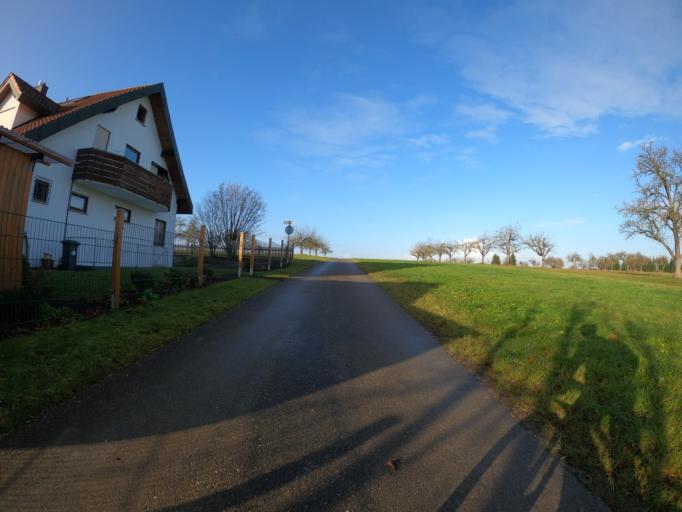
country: DE
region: Baden-Wuerttemberg
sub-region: Regierungsbezirk Stuttgart
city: Hattenhofen
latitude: 48.6703
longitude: 9.5680
